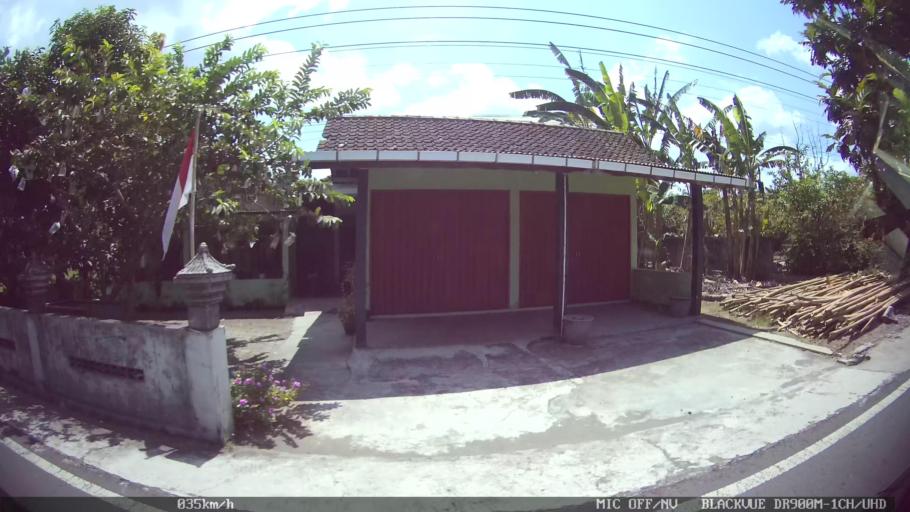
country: ID
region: Daerah Istimewa Yogyakarta
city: Bantul
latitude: -7.9053
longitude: 110.3364
